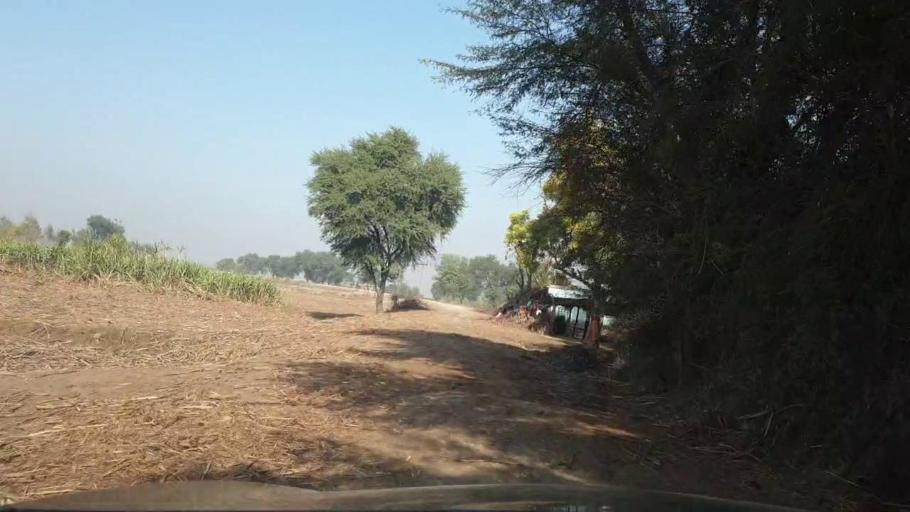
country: PK
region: Sindh
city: Ubauro
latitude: 28.1214
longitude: 69.7508
